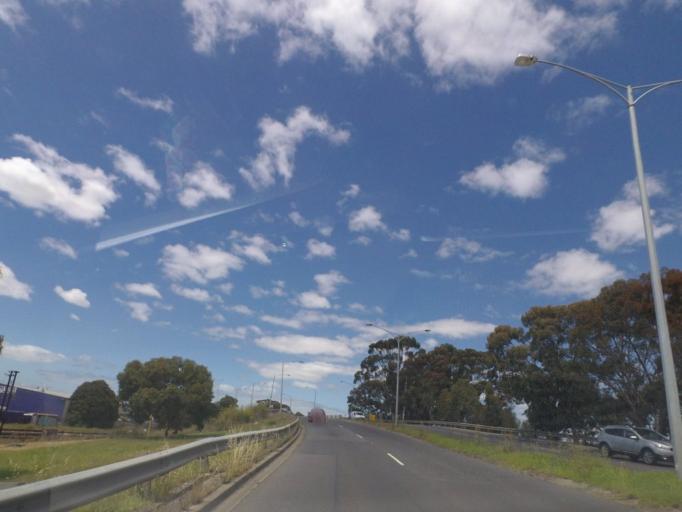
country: AU
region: Victoria
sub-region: Brimbank
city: Albion
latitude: -37.7627
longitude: 144.8312
